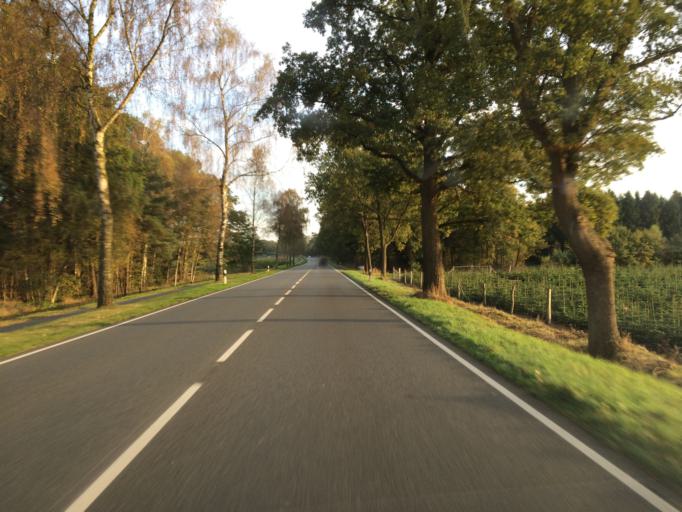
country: DE
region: Lower Saxony
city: Soltau
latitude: 52.9632
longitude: 9.8574
